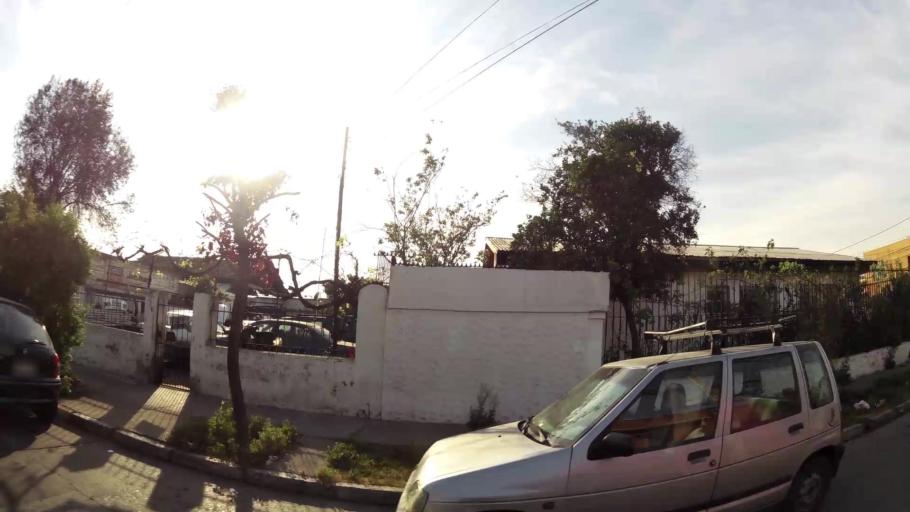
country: CL
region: Santiago Metropolitan
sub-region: Provincia de Santiago
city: Santiago
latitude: -33.5175
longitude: -70.6679
